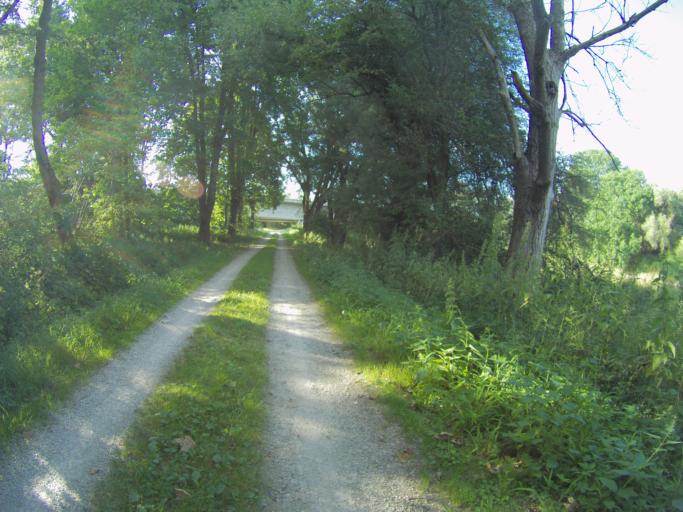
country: DE
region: Bavaria
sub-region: Upper Bavaria
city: Hallbergmoos
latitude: 48.3395
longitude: 11.7131
